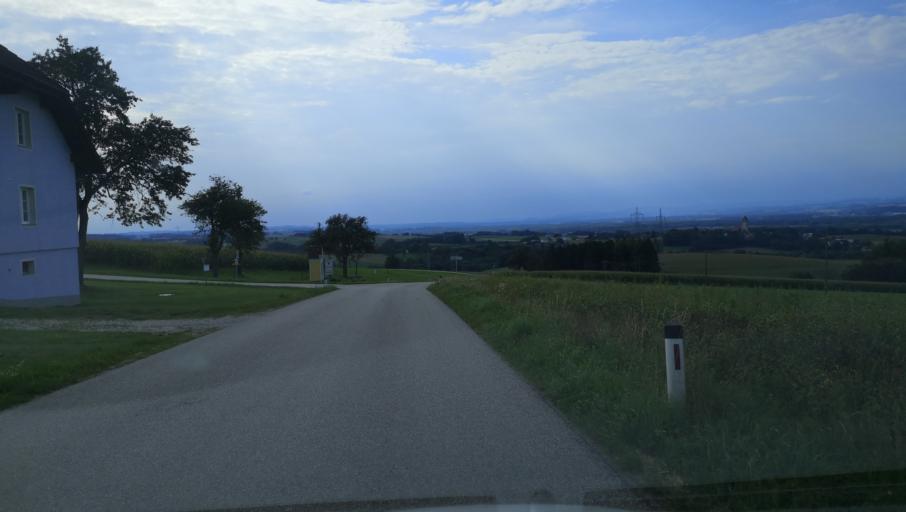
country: AT
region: Lower Austria
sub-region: Politischer Bezirk Amstetten
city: Amstetten
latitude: 48.1485
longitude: 14.8349
